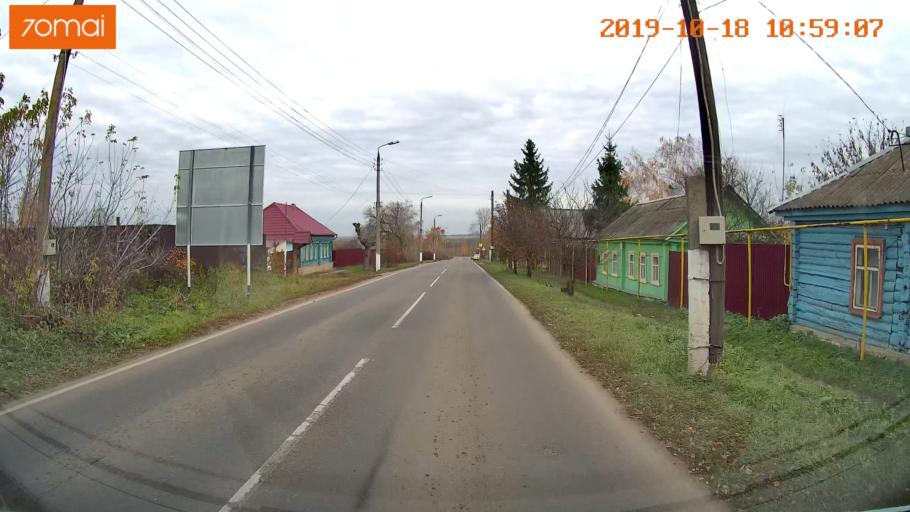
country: RU
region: Tula
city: Yepifan'
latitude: 53.8273
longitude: 38.5547
